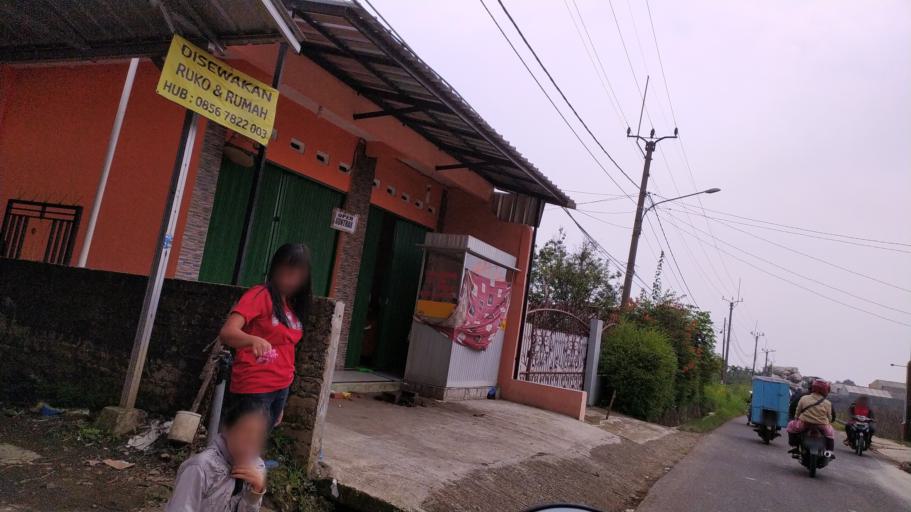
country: ID
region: West Java
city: Ciampea
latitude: -6.6017
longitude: 106.7026
